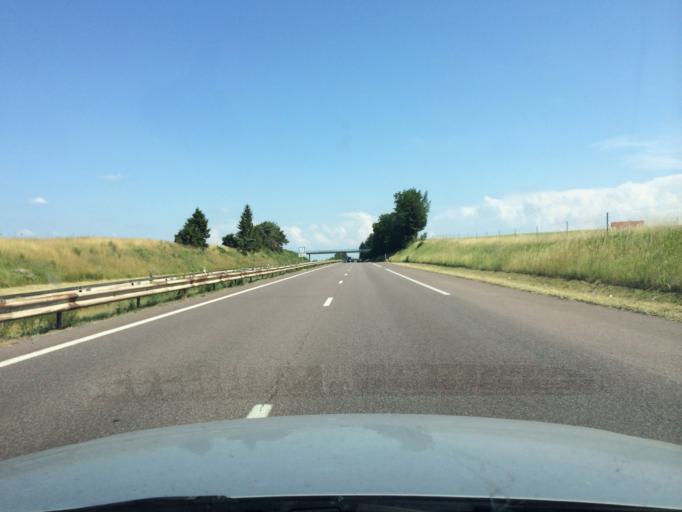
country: FR
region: Alsace
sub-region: Departement du Bas-Rhin
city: Mommenheim
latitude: 48.7662
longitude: 7.6507
